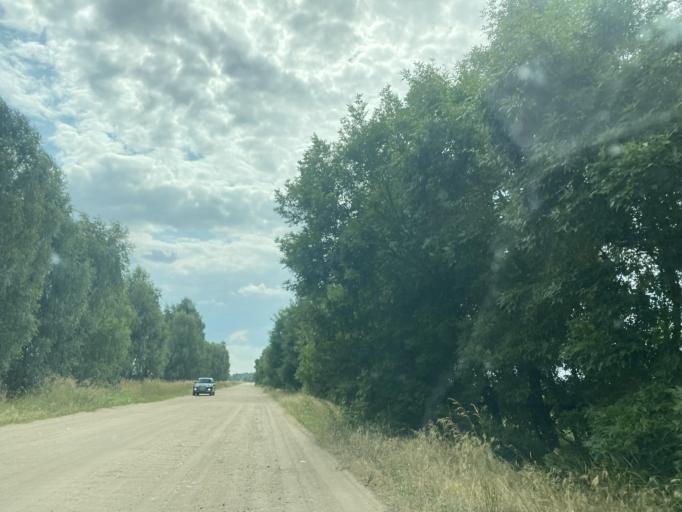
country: BY
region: Brest
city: Ivanava
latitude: 52.3609
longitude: 25.6354
